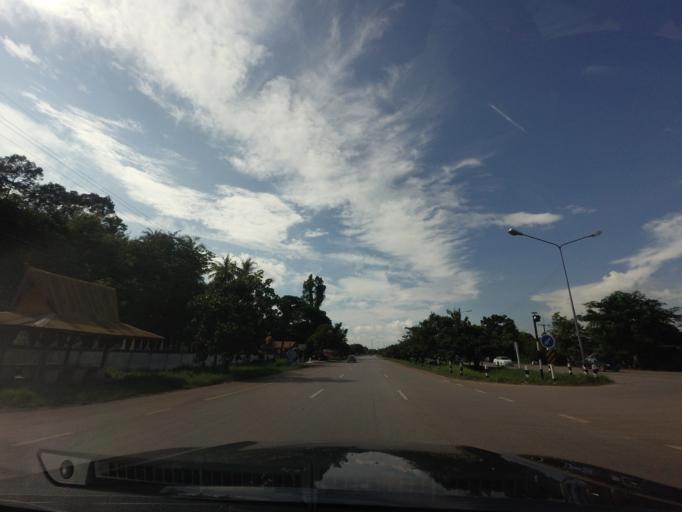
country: TH
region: Nong Khai
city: Sa Khrai
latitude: 17.6780
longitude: 102.7868
